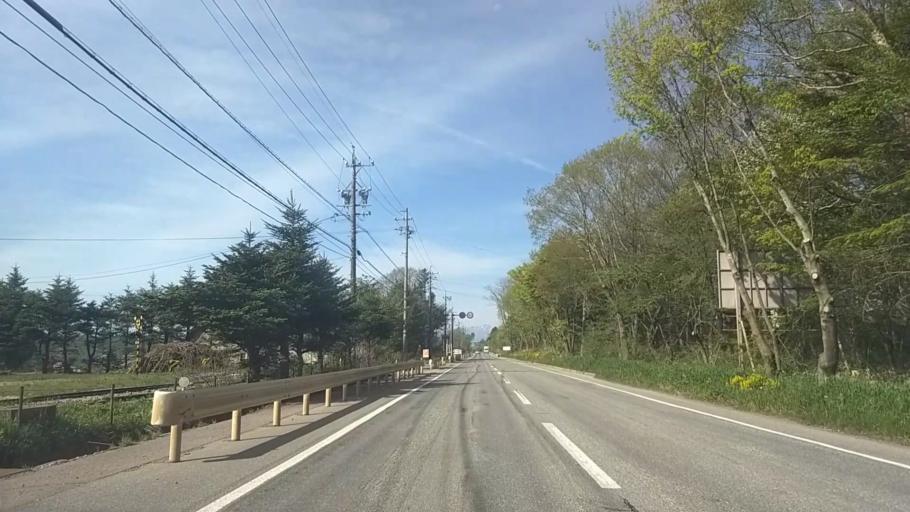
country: JP
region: Yamanashi
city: Nirasaki
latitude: 35.9540
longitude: 138.4616
